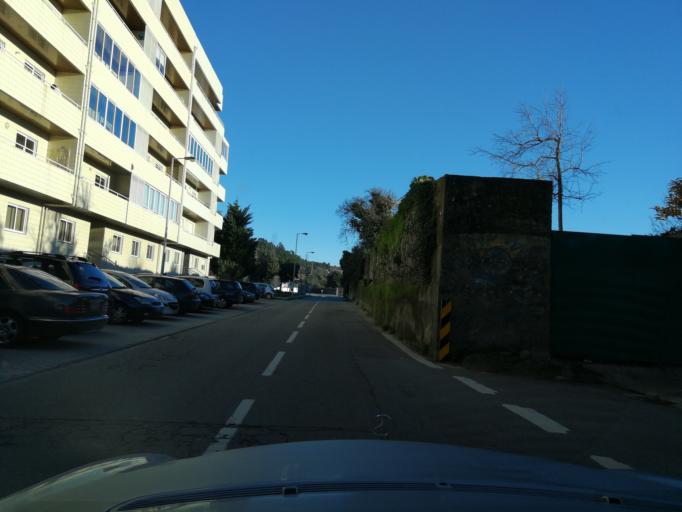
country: PT
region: Braga
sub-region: Braga
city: Braga
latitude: 41.5607
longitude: -8.4138
